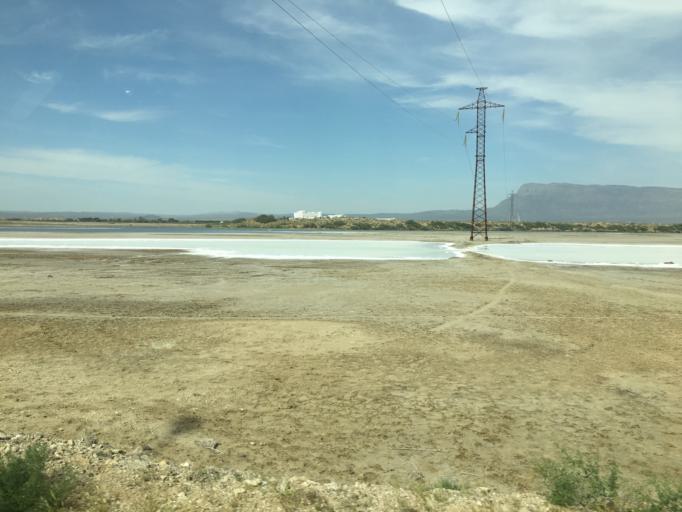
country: TM
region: Balkan
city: Balkanabat
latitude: 39.6175
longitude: 54.1642
